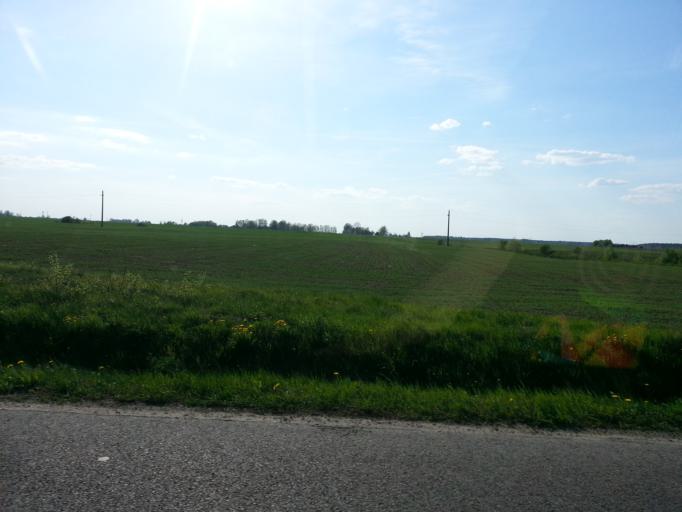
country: LT
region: Panevezys
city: Pasvalys
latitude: 55.9395
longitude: 24.3369
